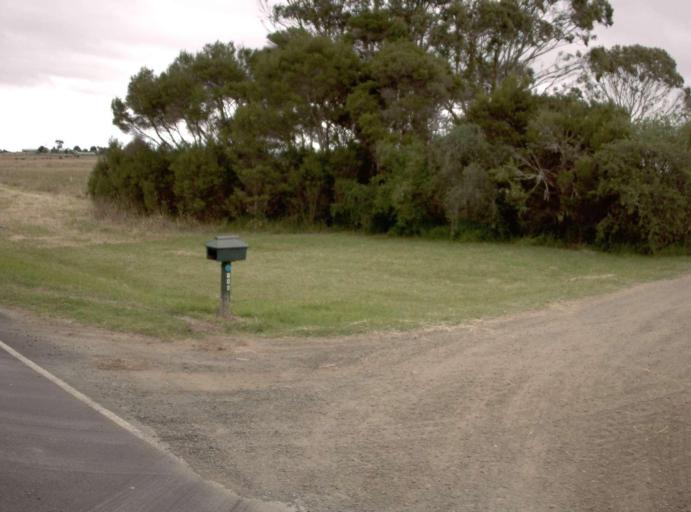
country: AU
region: Victoria
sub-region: Wellington
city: Sale
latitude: -38.5465
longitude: 146.8866
